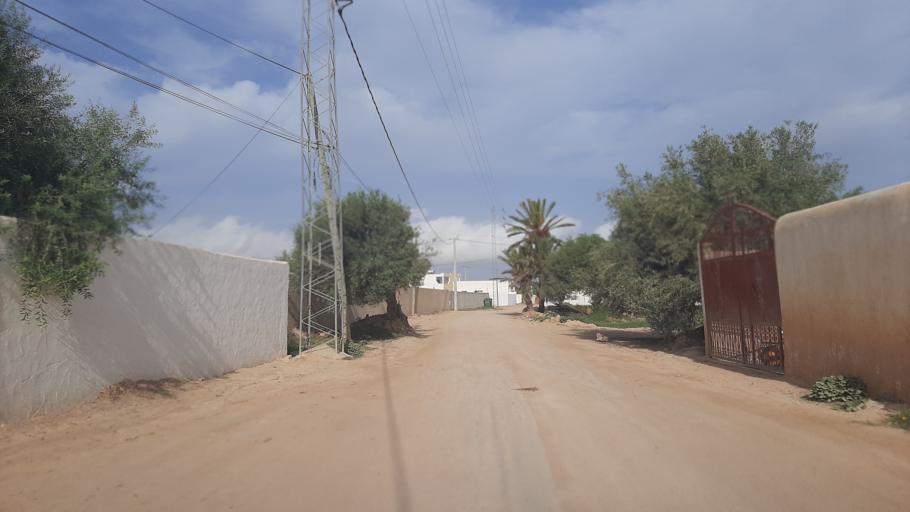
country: TN
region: Madanin
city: Midoun
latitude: 33.7985
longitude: 11.0285
